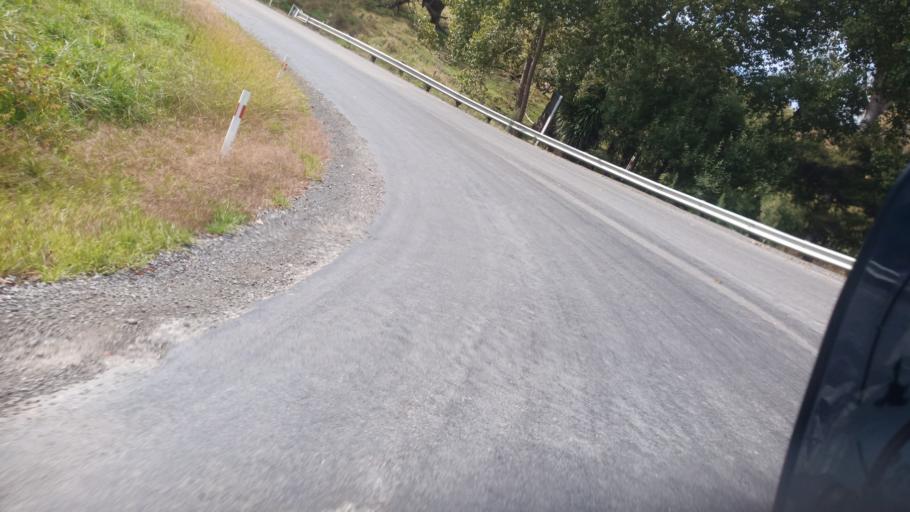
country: NZ
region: Gisborne
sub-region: Gisborne District
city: Gisborne
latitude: -38.1573
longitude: 178.2862
